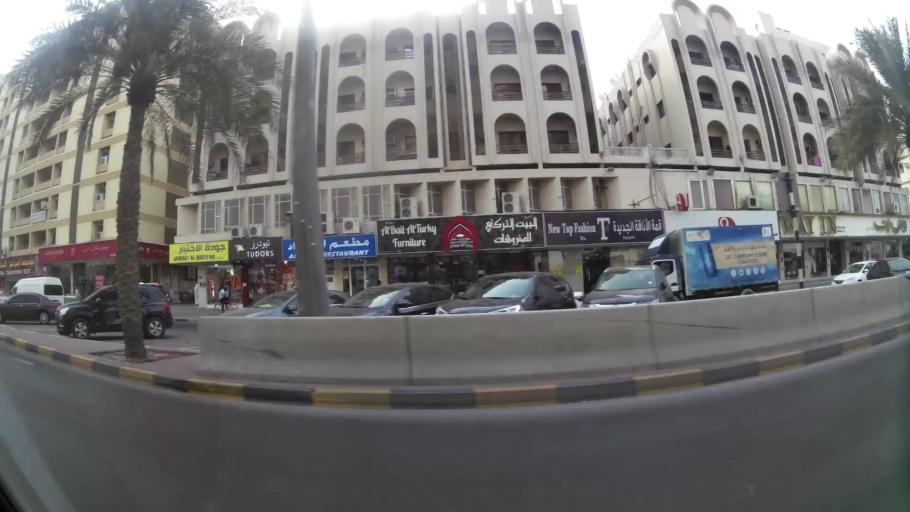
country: AE
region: Ash Shariqah
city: Sharjah
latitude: 25.3187
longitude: 55.3861
